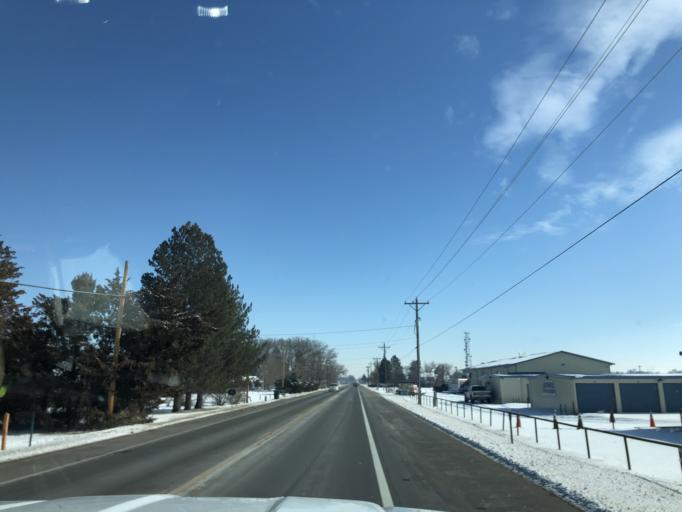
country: US
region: Colorado
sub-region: Morgan County
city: Fort Morgan
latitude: 40.2539
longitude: -103.8241
